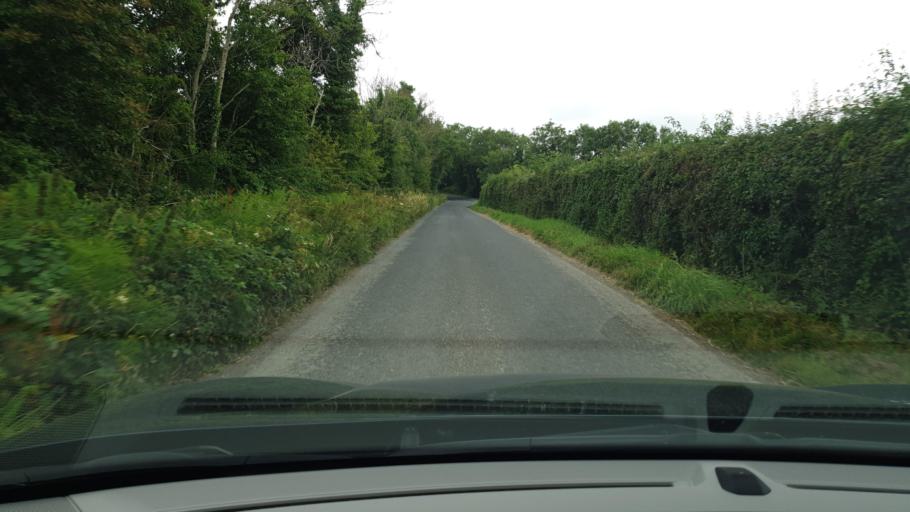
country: IE
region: Leinster
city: Balrothery
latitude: 53.5719
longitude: -6.1997
